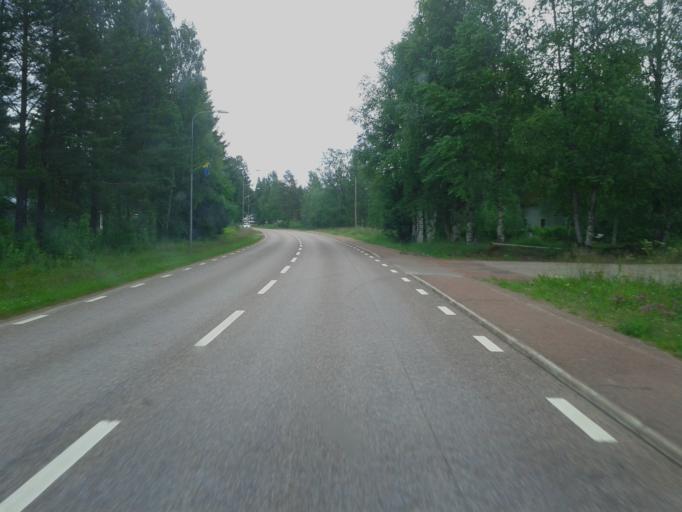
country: NO
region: Hedmark
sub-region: Trysil
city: Innbygda
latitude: 61.6948
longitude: 13.1178
